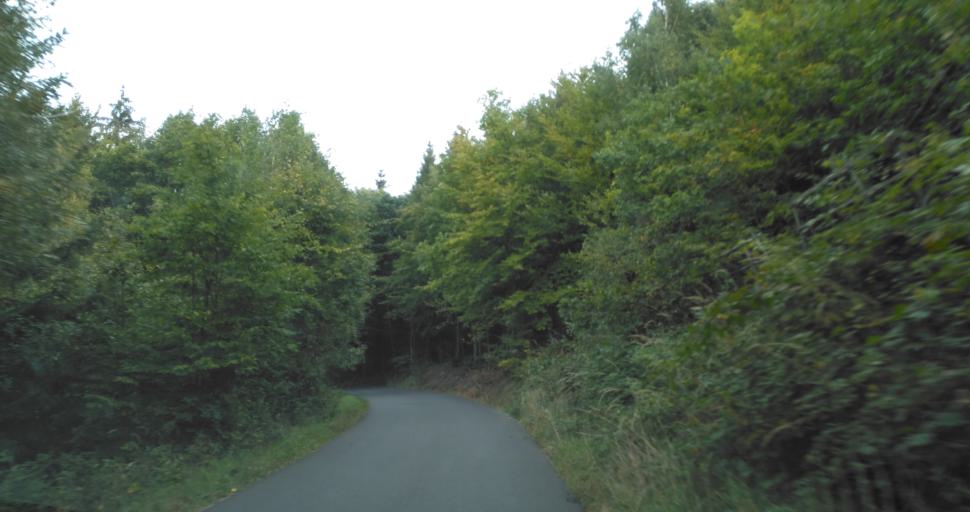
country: CZ
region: Plzensky
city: Zbiroh
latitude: 49.9378
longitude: 13.7807
